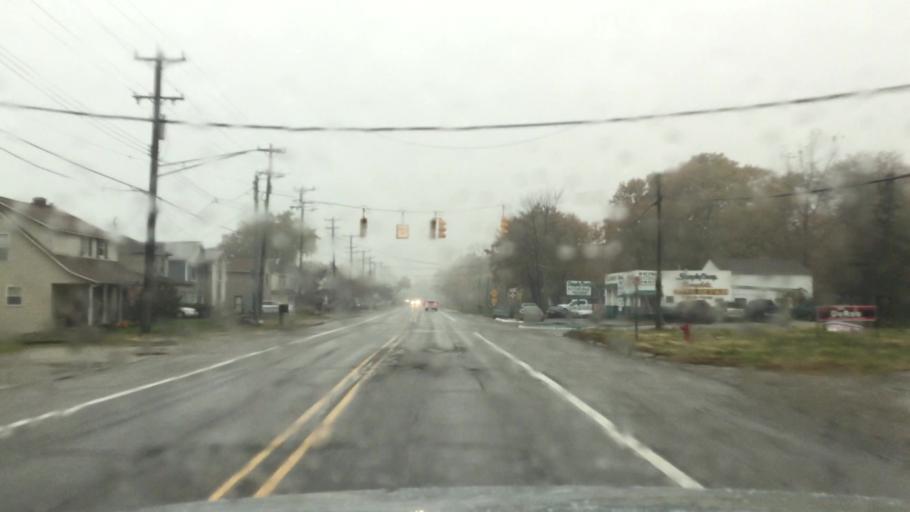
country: US
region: Michigan
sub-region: Macomb County
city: New Baltimore
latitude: 42.6846
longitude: -82.6683
